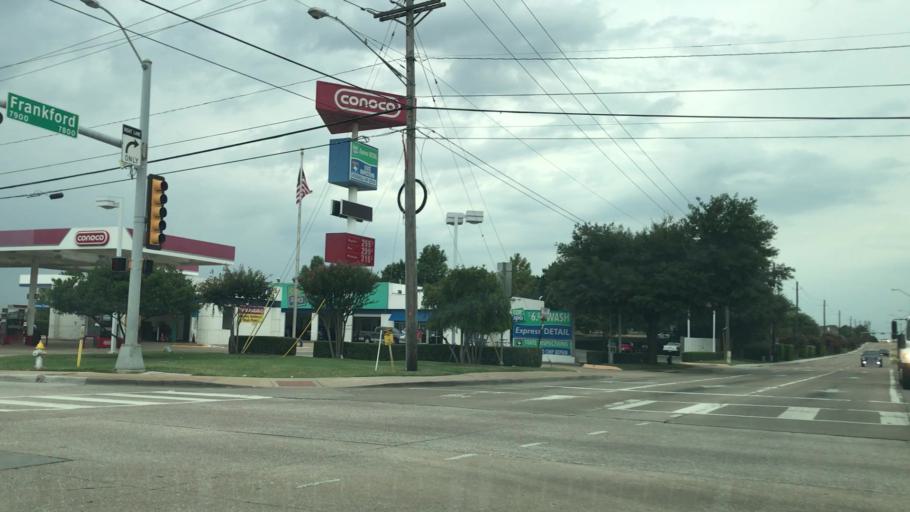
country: US
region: Texas
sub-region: Dallas County
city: Richardson
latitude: 32.9976
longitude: -96.7678
